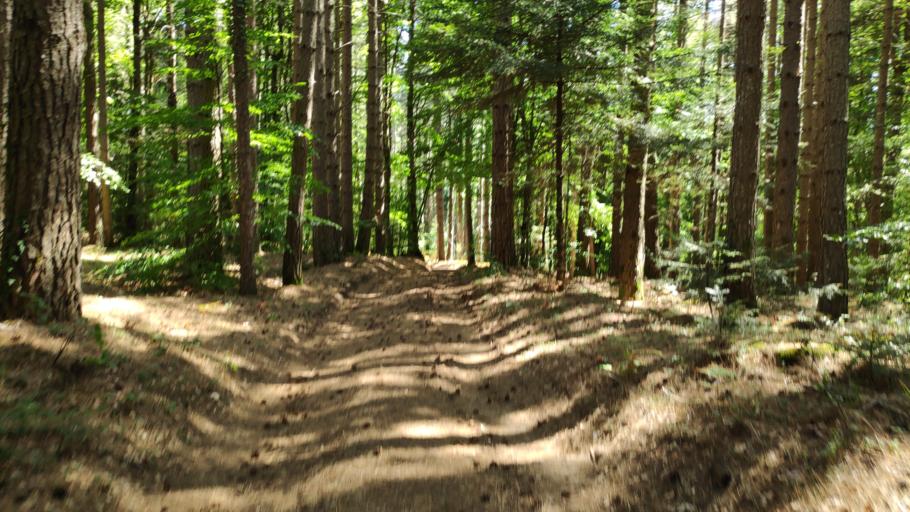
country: IT
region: Calabria
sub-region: Provincia di Vibo-Valentia
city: Mongiana
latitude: 38.5301
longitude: 16.3783
